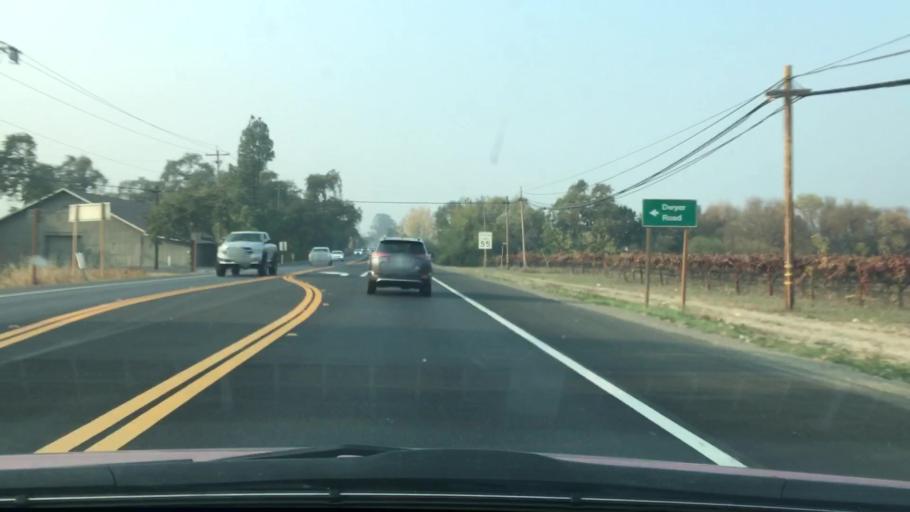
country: US
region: California
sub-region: Napa County
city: Yountville
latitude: 38.4231
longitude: -122.3906
